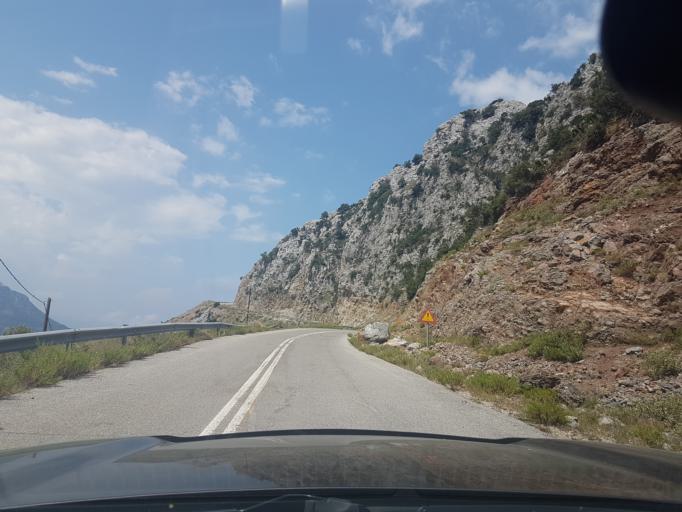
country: GR
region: Central Greece
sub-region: Nomos Evvoias
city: Kymi
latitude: 38.6526
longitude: 23.9686
